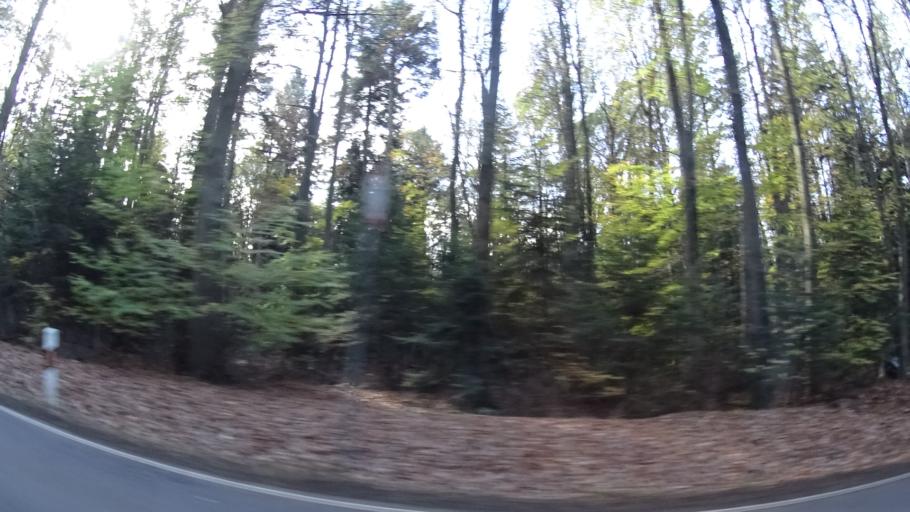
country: DE
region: Baden-Wuerttemberg
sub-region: Karlsruhe Region
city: Pforzheim
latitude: 48.8743
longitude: 8.7200
